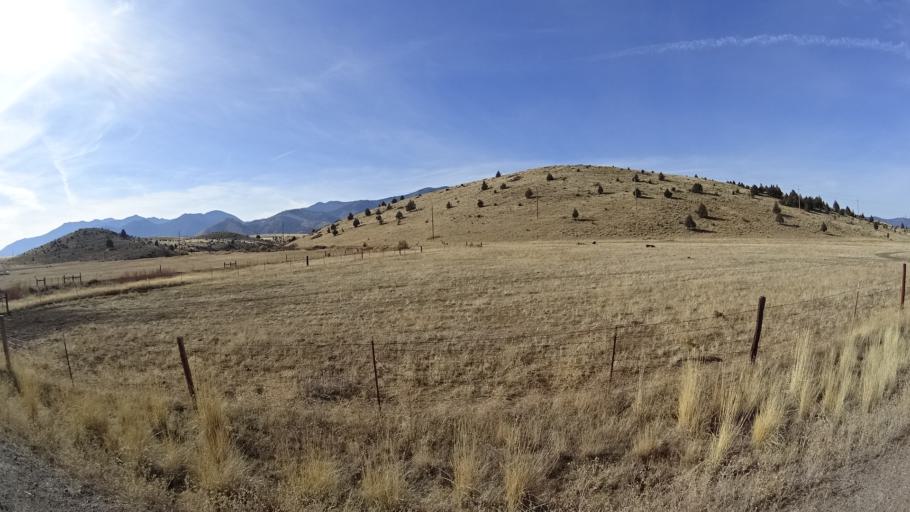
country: US
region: California
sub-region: Siskiyou County
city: Weed
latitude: 41.5043
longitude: -122.4566
